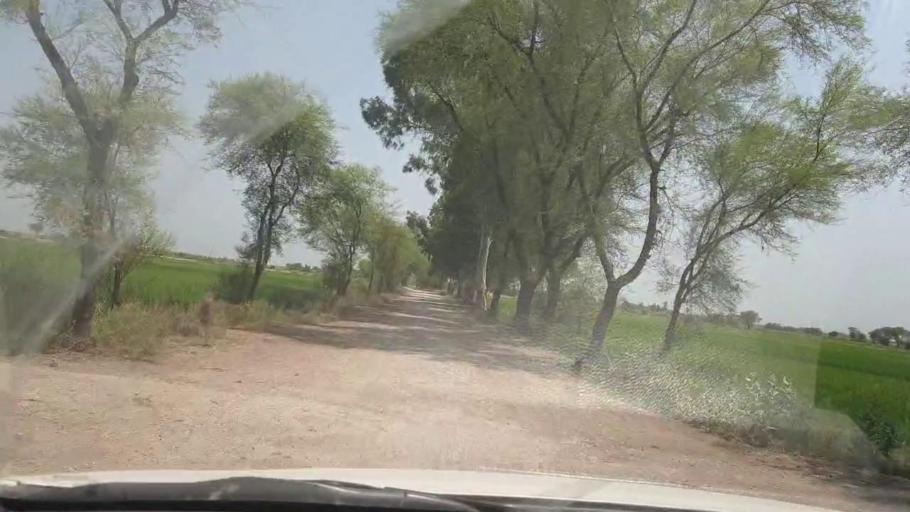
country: PK
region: Sindh
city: Lakhi
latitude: 27.8831
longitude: 68.7427
